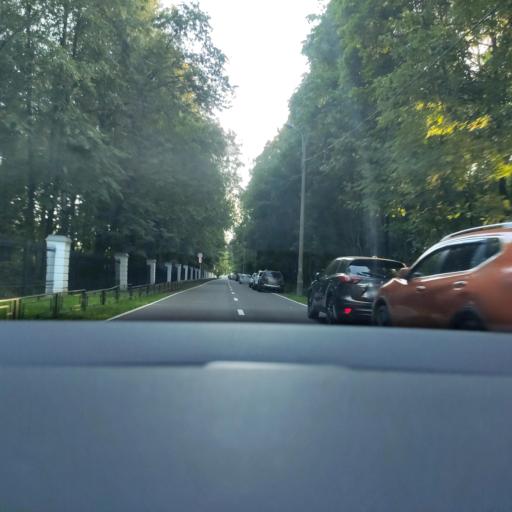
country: RU
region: Moscow
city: Perovo
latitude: 55.7384
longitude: 37.8066
